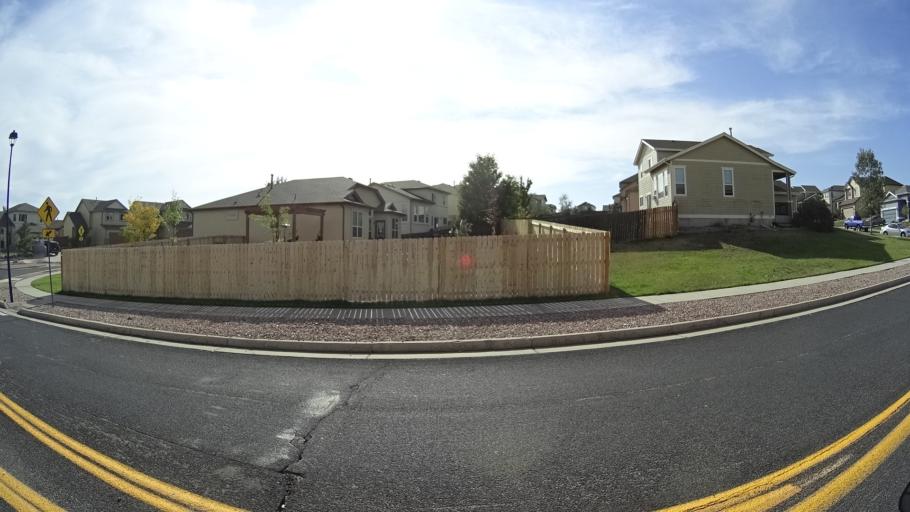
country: US
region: Colorado
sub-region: El Paso County
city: Cimarron Hills
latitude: 38.9070
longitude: -104.6854
